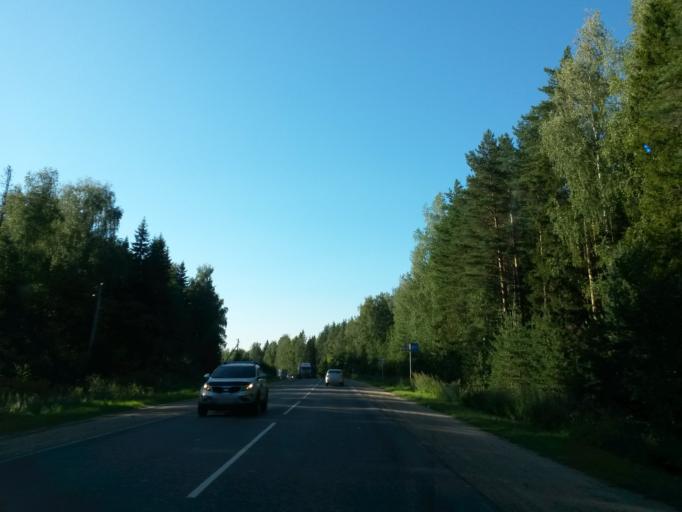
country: RU
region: Ivanovo
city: Novo-Talitsy
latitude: 57.0514
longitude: 40.7355
